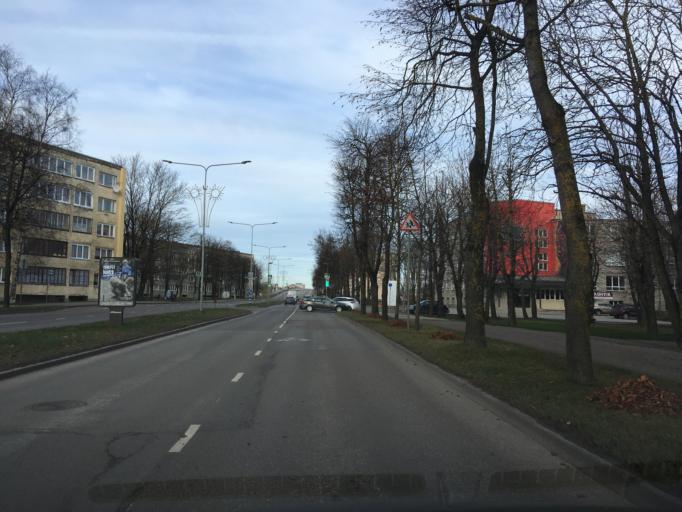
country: EE
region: Ida-Virumaa
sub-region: Narva linn
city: Narva
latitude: 59.3679
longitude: 28.1864
